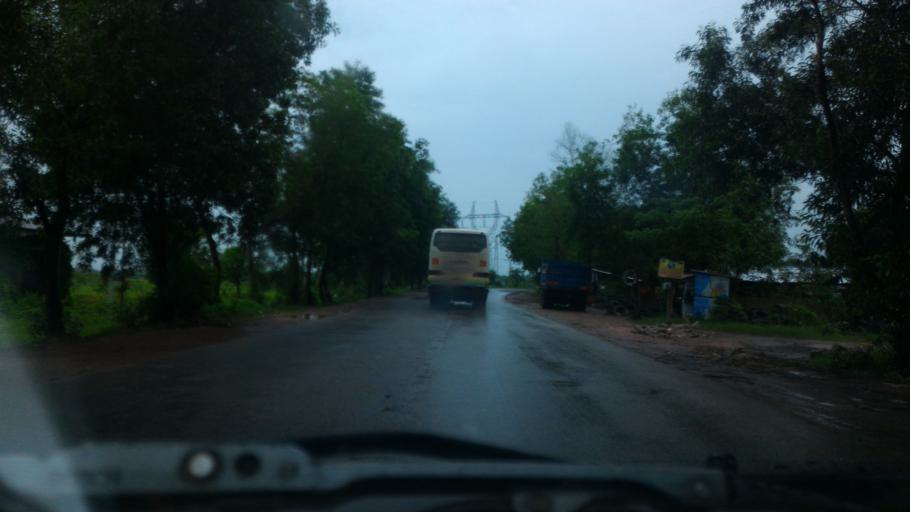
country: MM
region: Bago
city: Thanatpin
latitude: 17.1741
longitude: 95.9875
